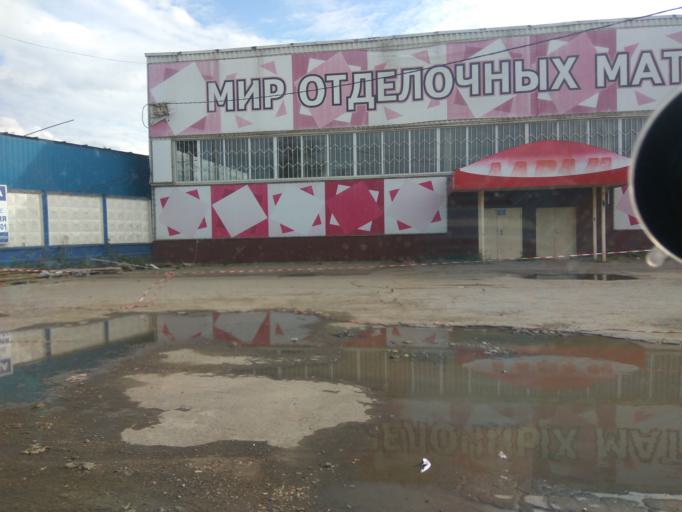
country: RU
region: Moskovskaya
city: Ramenskoye
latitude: 55.5664
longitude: 38.2706
